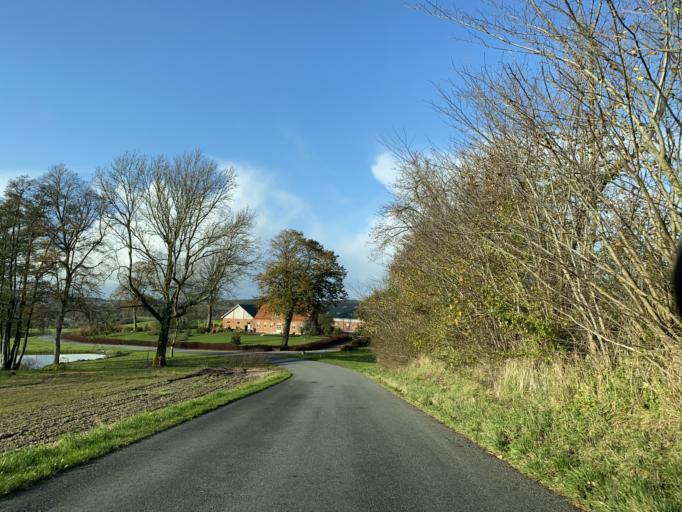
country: DK
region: Central Jutland
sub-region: Viborg Kommune
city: Bjerringbro
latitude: 56.3706
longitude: 9.7161
